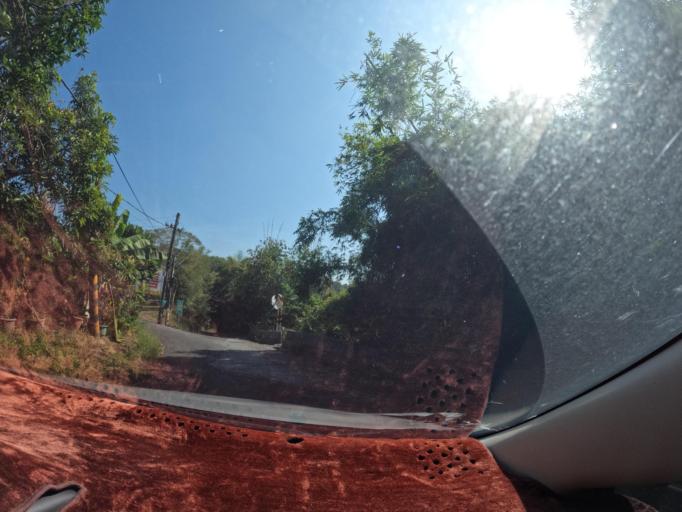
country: TW
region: Taiwan
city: Yujing
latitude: 23.0474
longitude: 120.3773
